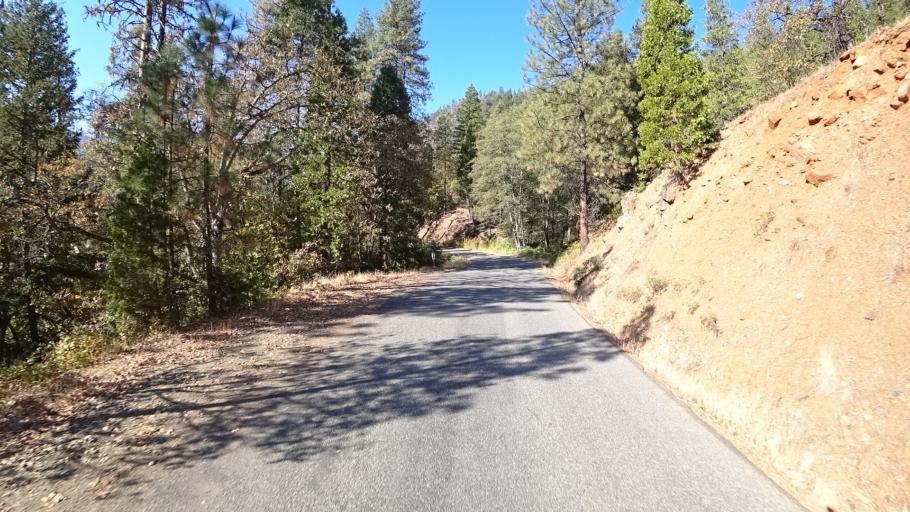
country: US
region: California
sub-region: Siskiyou County
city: Happy Camp
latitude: 41.7057
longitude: -123.0348
